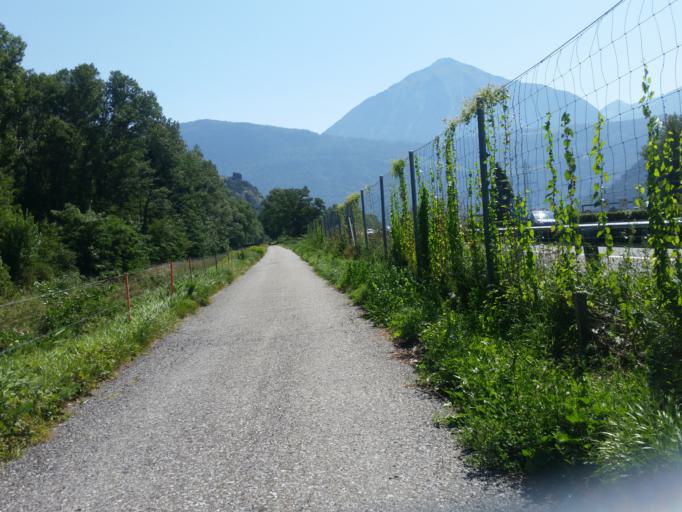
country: CH
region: Valais
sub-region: Saint-Maurice District
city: Vernayaz
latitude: 46.1303
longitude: 7.0590
